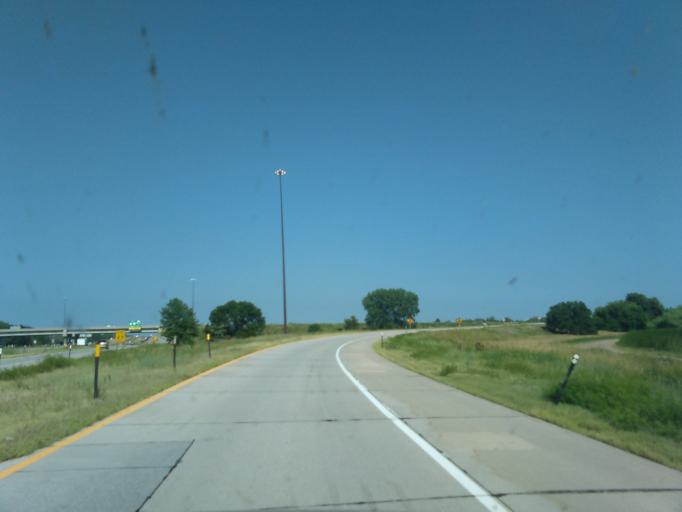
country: US
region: Nebraska
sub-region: Hall County
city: Grand Island
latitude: 40.8192
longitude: -98.3819
